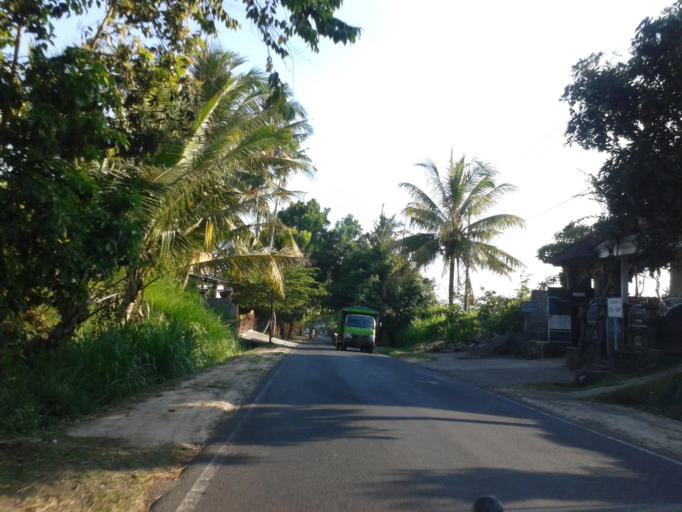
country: ID
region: Bali
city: Klungkung
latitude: -8.5086
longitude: 115.4025
